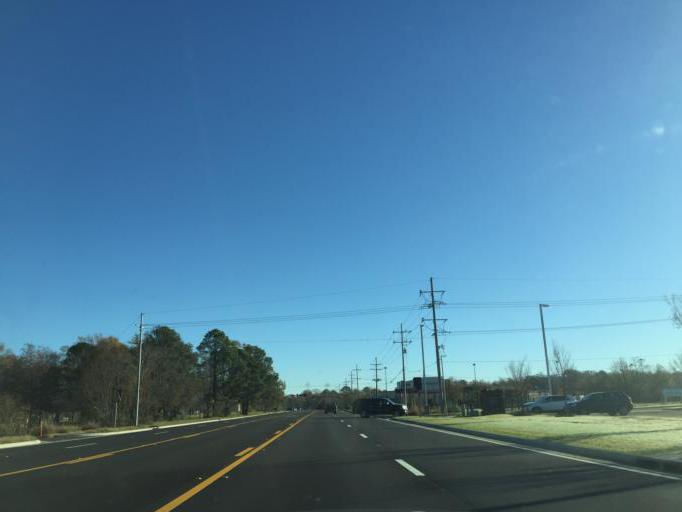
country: US
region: Mississippi
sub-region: Rankin County
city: Flowood
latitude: 32.3230
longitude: -90.1103
